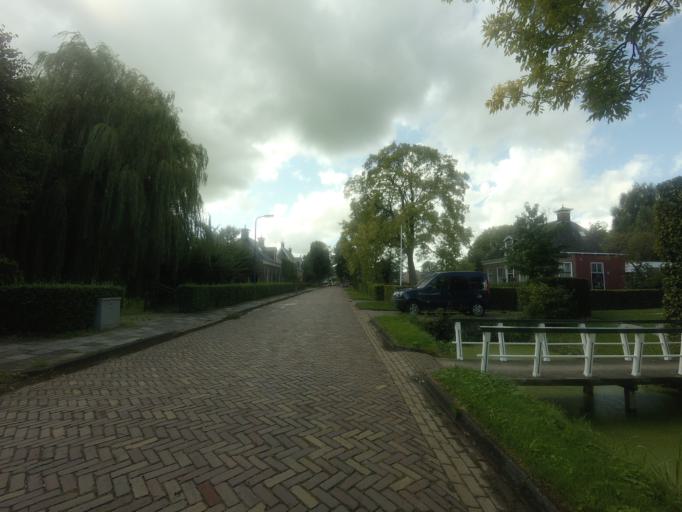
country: NL
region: Friesland
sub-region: Gemeente Littenseradiel
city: Makkum
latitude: 53.0890
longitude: 5.6984
